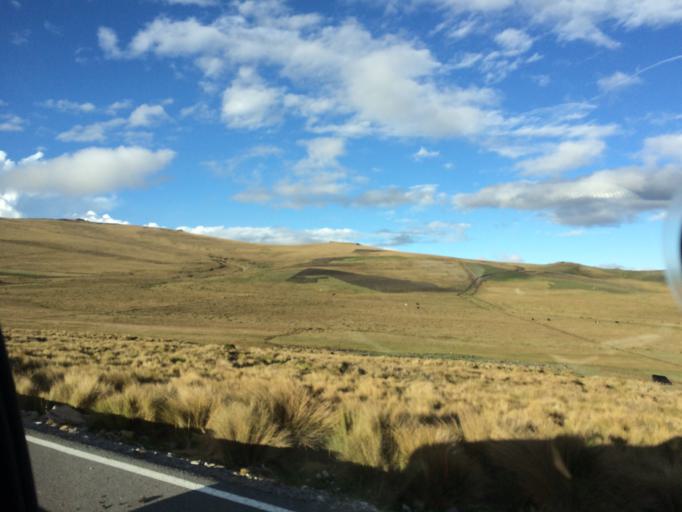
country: EC
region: Chimborazo
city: Alausi
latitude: -2.2312
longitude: -78.6844
